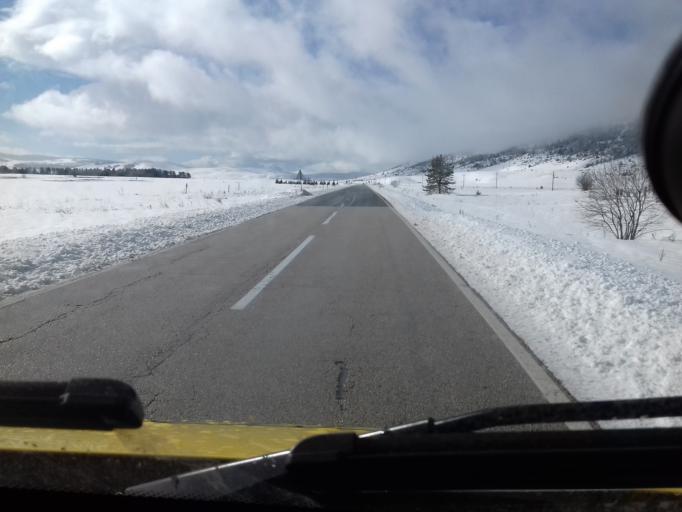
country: BA
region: Federation of Bosnia and Herzegovina
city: Tomislavgrad
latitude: 43.9306
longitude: 17.2093
